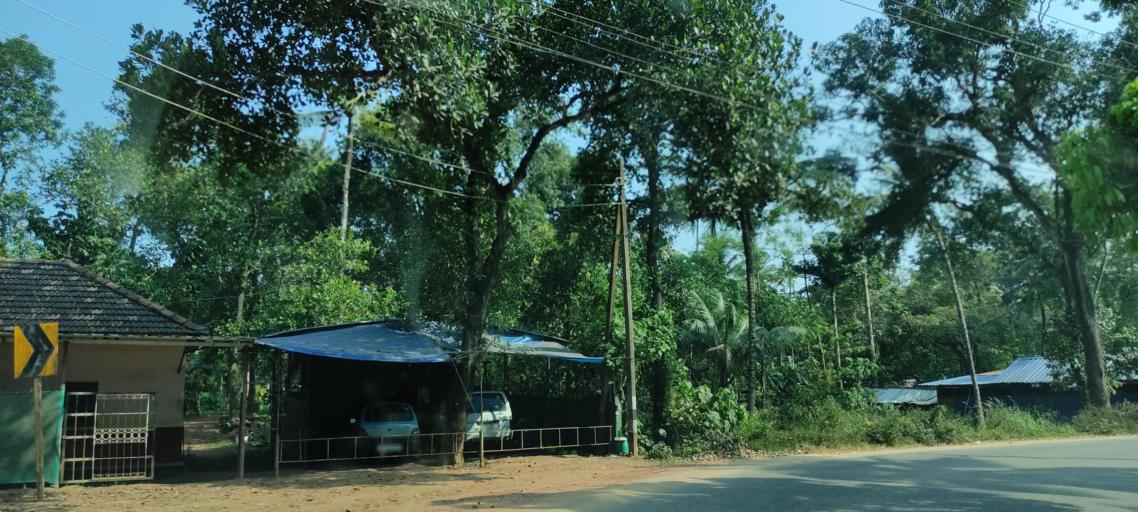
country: IN
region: Kerala
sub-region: Kollam
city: Panmana
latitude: 9.0456
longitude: 76.5761
